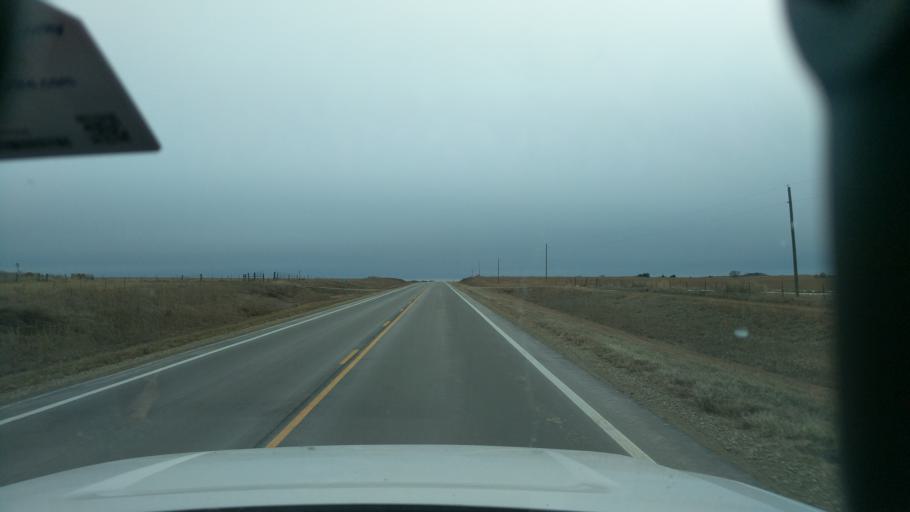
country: US
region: Kansas
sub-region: Dickinson County
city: Herington
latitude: 38.7623
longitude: -96.9274
